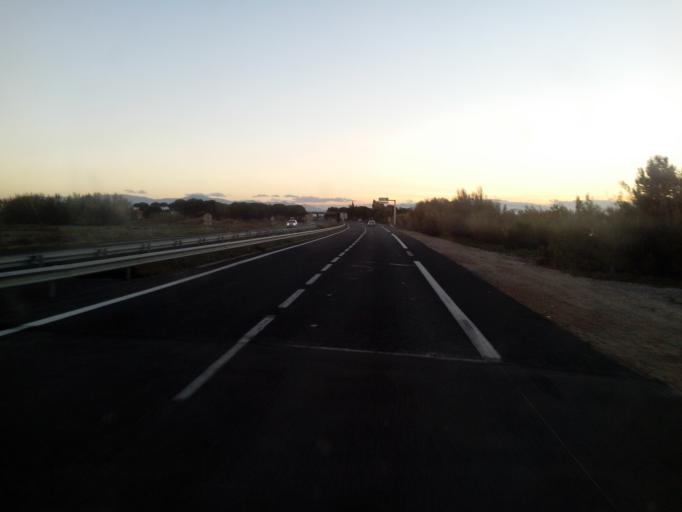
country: FR
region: Languedoc-Roussillon
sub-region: Departement des Pyrenees-Orientales
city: Le Barcares
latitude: 42.7968
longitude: 3.0272
